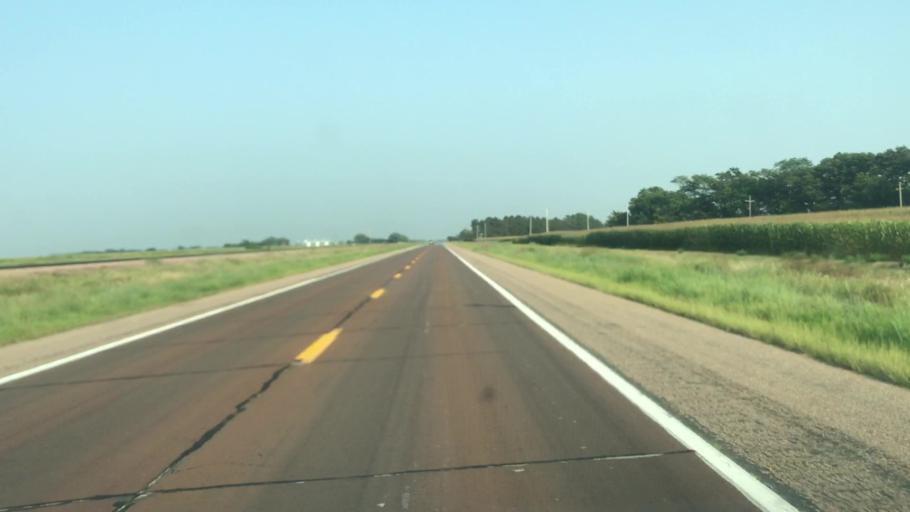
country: US
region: Nebraska
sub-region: Hall County
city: Wood River
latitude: 40.9905
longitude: -98.5539
